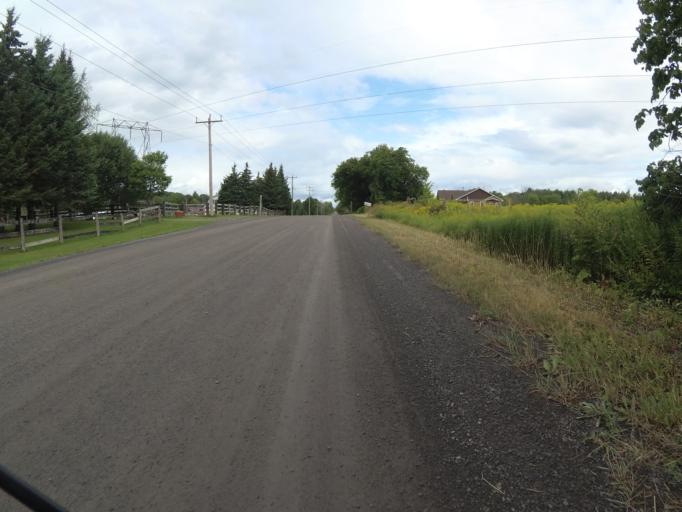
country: CA
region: Ontario
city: Clarence-Rockland
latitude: 45.4662
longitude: -75.3011
